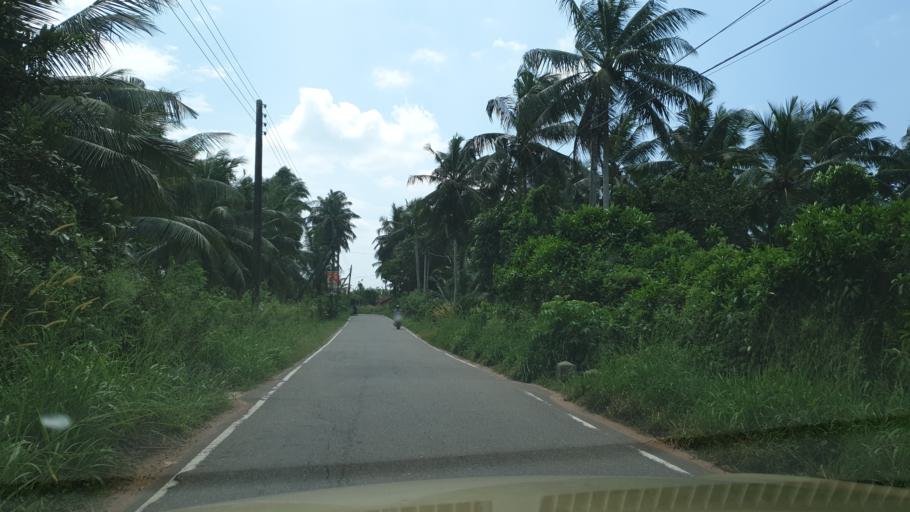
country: LK
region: North Western
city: Kuliyapitiya
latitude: 7.3554
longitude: 79.9675
